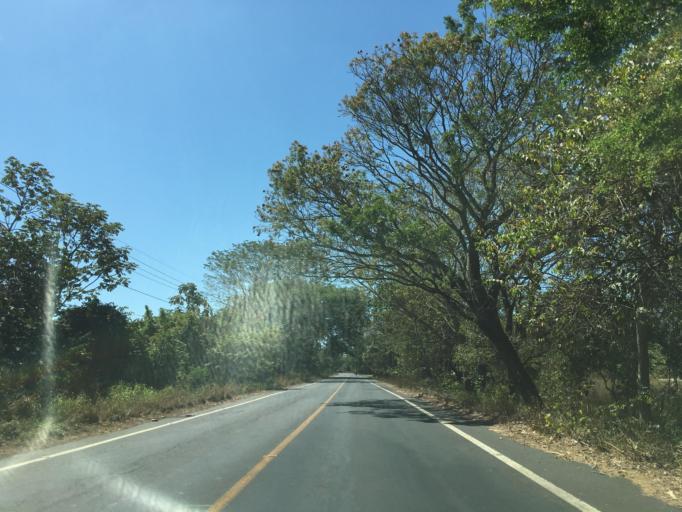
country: GT
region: Escuintla
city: Puerto San Jose
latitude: 13.9871
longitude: -90.8934
